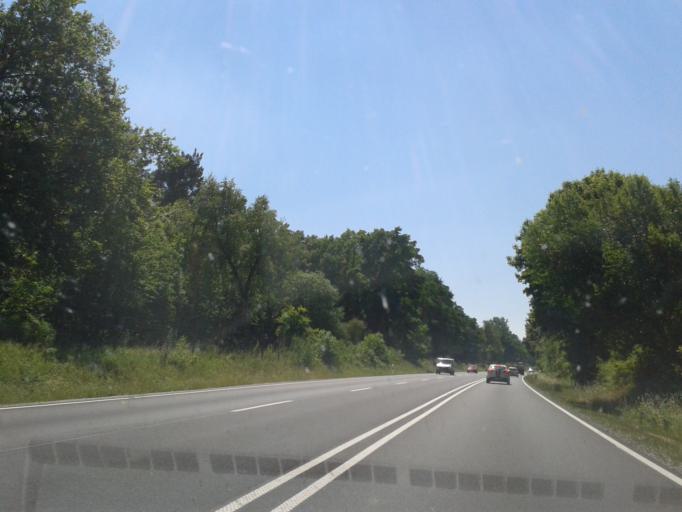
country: DE
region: North Rhine-Westphalia
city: Bad Lippspringe
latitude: 51.7861
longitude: 8.7927
